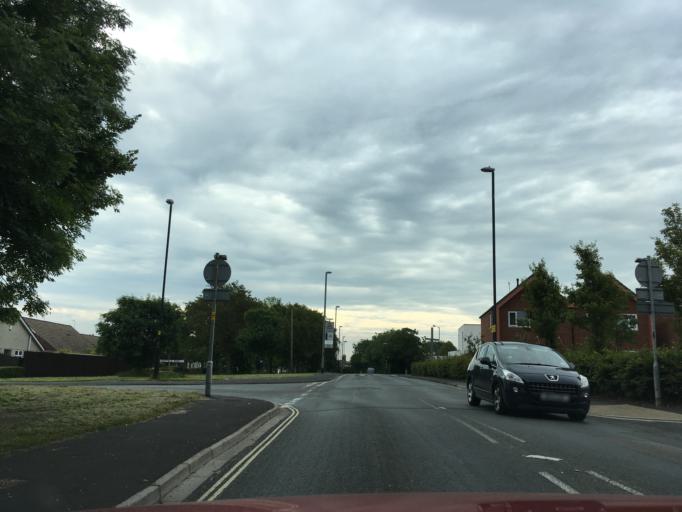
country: GB
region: England
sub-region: Bath and North East Somerset
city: Whitchurch
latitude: 51.4072
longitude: -2.5719
